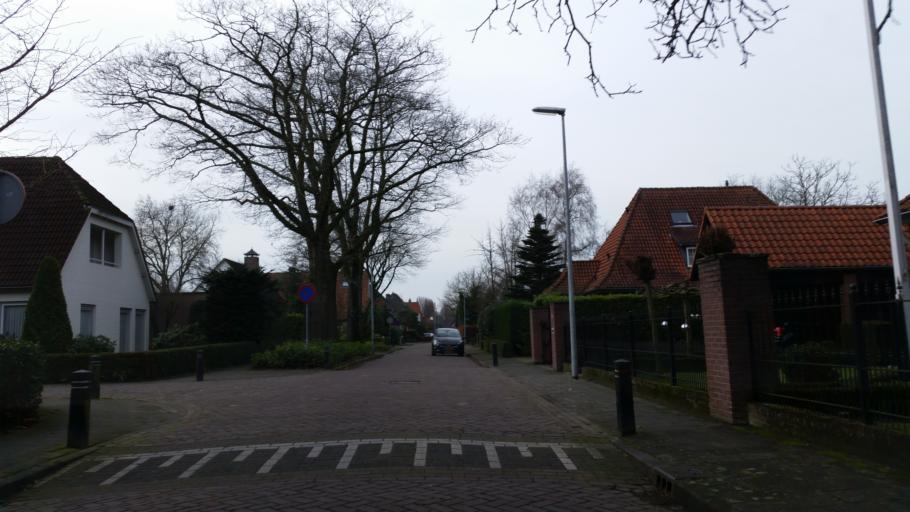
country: NL
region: North Brabant
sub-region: Gemeente Eindhoven
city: Meerhoven
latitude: 51.4286
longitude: 5.4224
